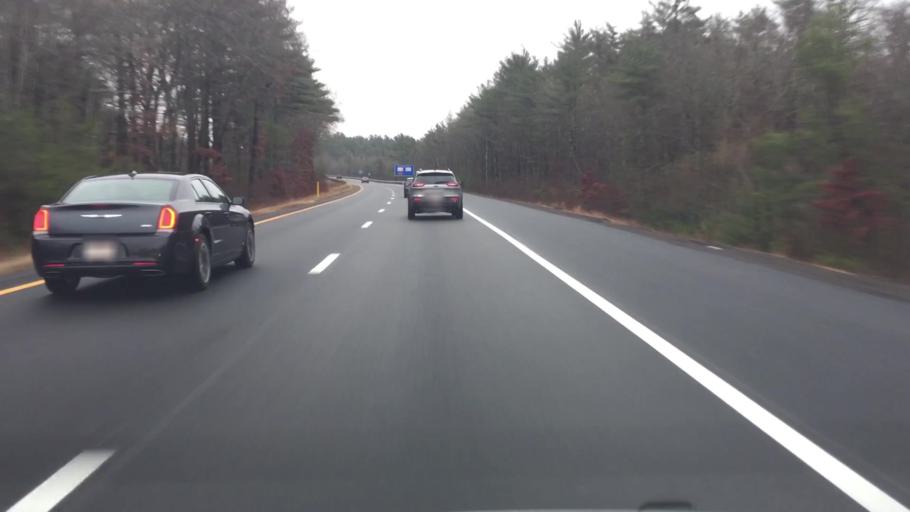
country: US
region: Massachusetts
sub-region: Plymouth County
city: West Wareham
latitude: 41.8146
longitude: -70.7960
